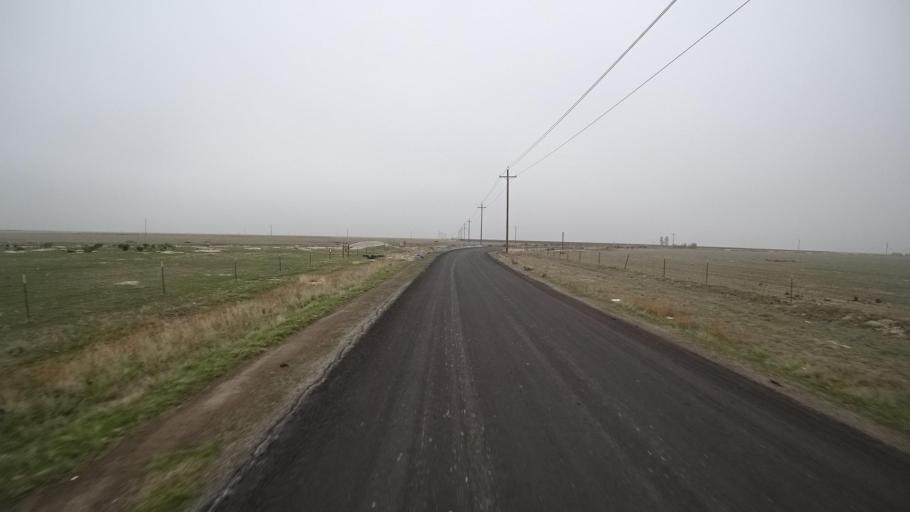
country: US
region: California
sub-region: Tulare County
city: Alpaugh
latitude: 35.7702
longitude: -119.4723
